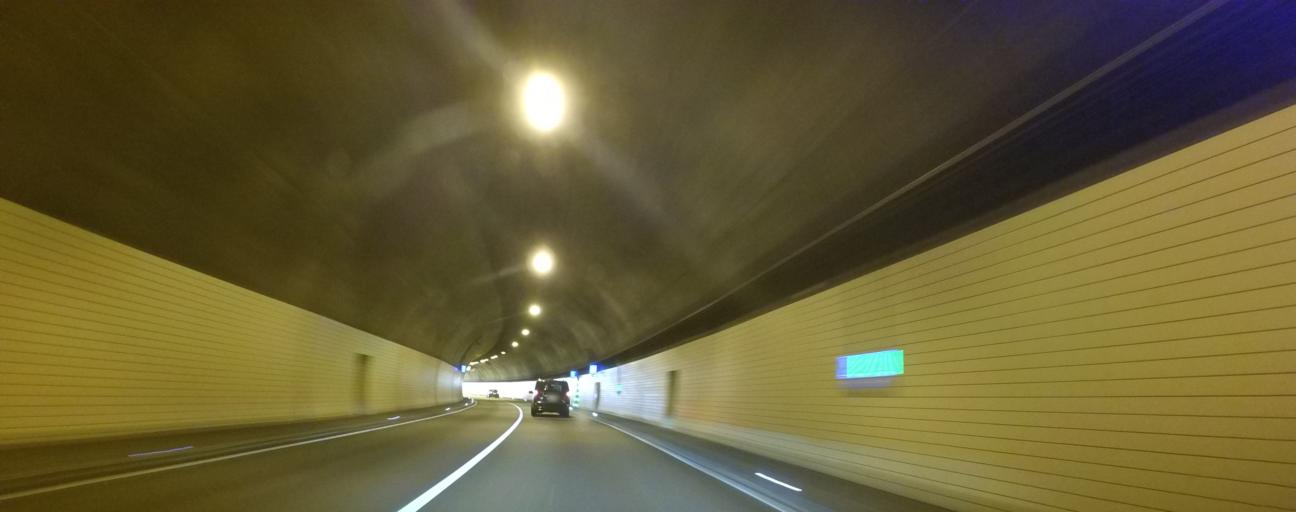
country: DE
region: Rheinland-Pfalz
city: Wernersberg
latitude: 49.2075
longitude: 7.9426
